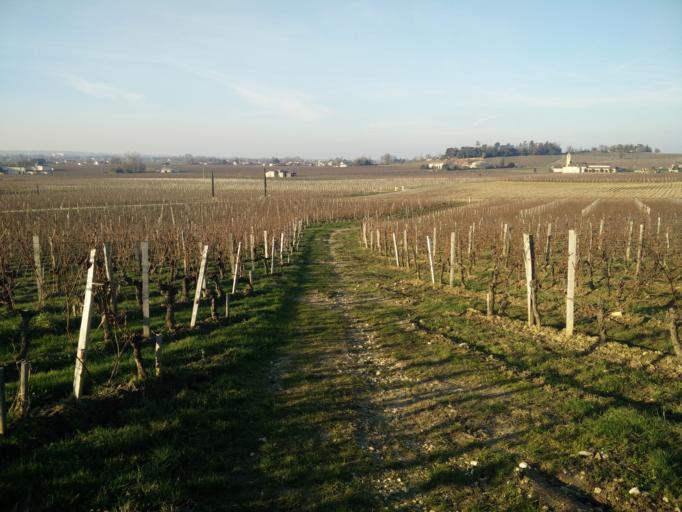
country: FR
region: Aquitaine
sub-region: Departement de la Gironde
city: Saint-Emilion
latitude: 44.8859
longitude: -0.1692
